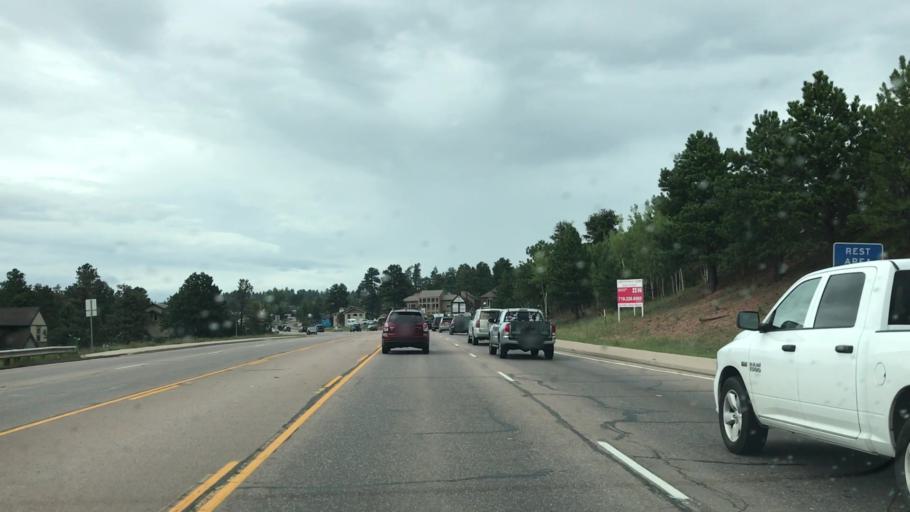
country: US
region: Colorado
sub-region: Teller County
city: Woodland Park
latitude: 38.9854
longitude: -105.0457
